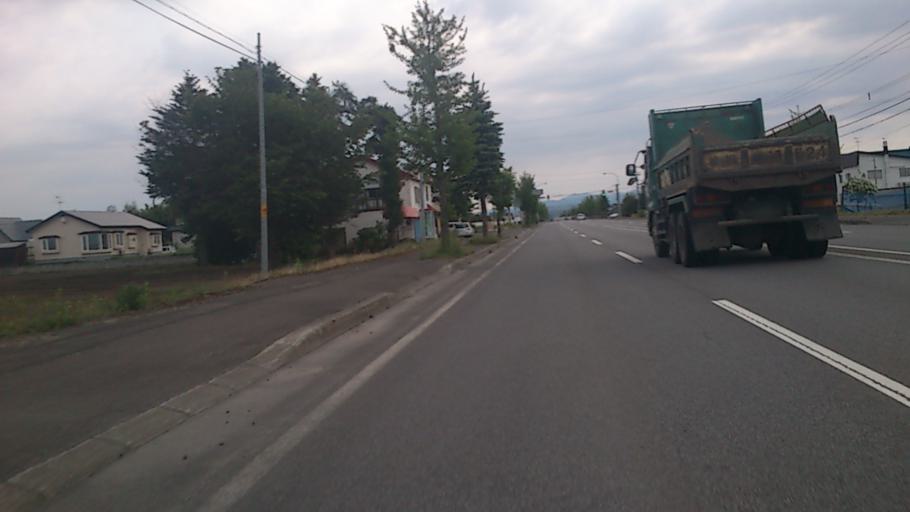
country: JP
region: Hokkaido
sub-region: Asahikawa-shi
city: Asahikawa
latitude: 43.8372
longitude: 142.4766
